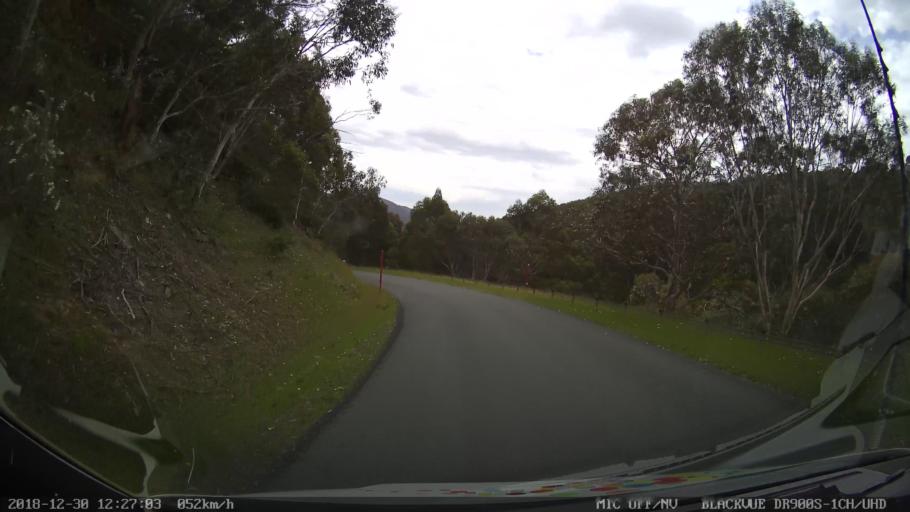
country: AU
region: New South Wales
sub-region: Snowy River
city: Jindabyne
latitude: -36.3339
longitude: 148.4903
